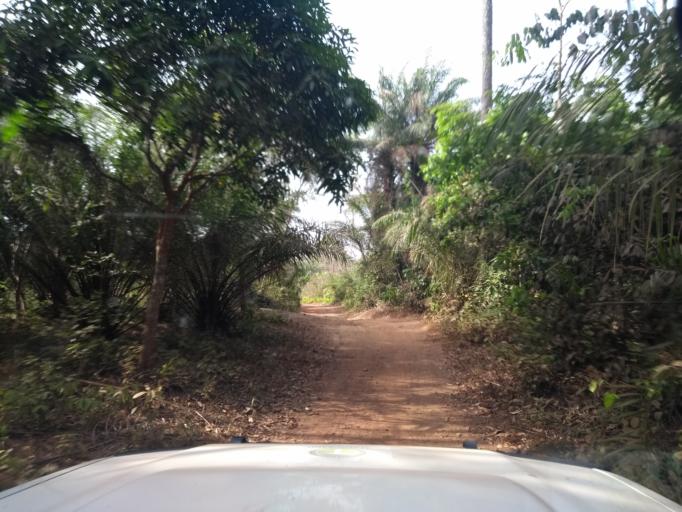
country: GN
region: Kindia
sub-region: Prefecture de Dubreka
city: Dubreka
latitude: 9.8360
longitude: -13.5584
